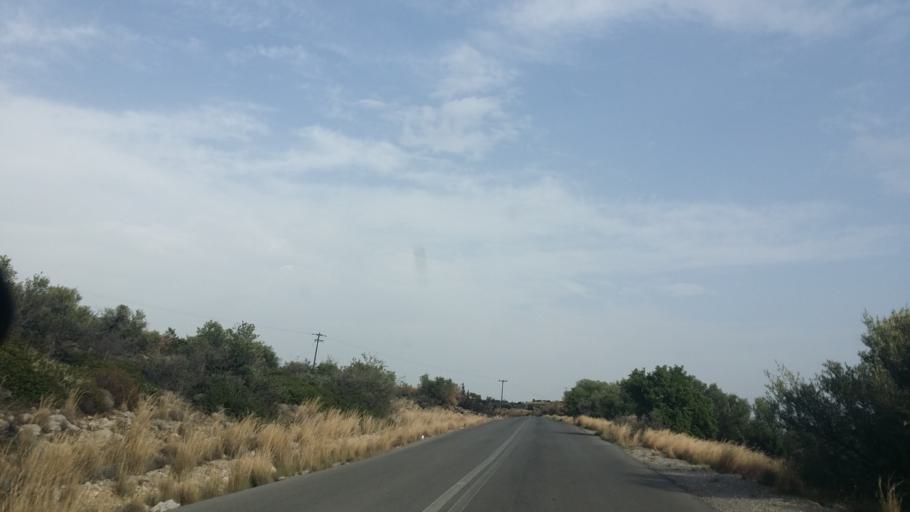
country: GR
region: Central Greece
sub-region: Nomos Voiotias
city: Korini
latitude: 38.2561
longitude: 22.8899
